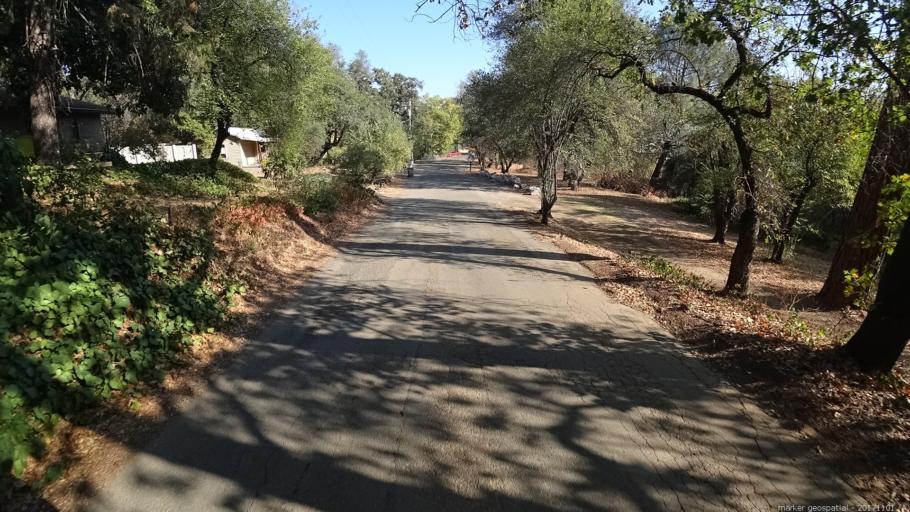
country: US
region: California
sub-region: Shasta County
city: Shasta Lake
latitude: 40.7145
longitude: -122.3344
